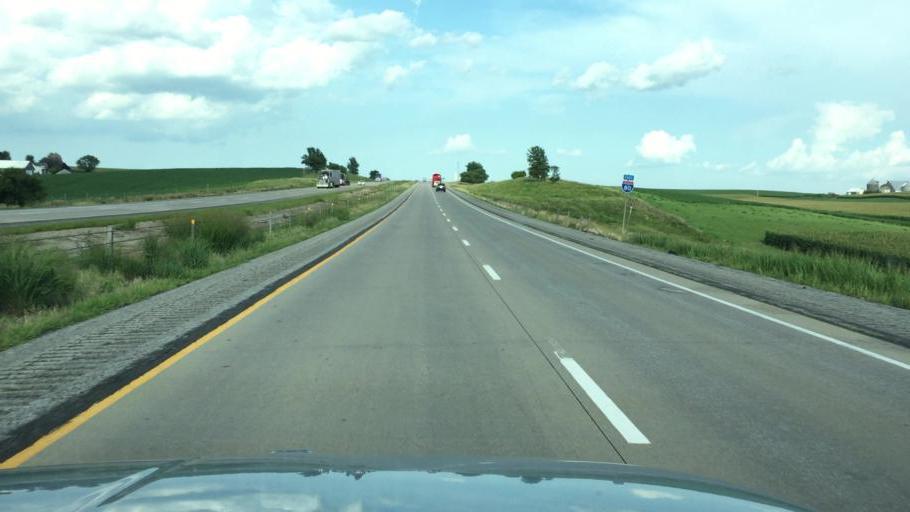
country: US
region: Iowa
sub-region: Iowa County
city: Williamsburg
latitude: 41.6870
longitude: -91.9953
